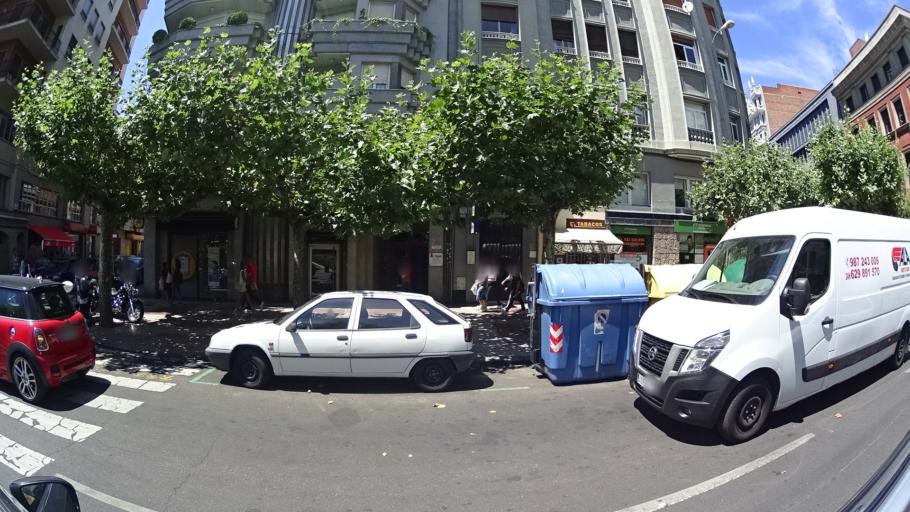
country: ES
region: Castille and Leon
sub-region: Provincia de Leon
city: Leon
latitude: 42.5995
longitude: -5.5764
